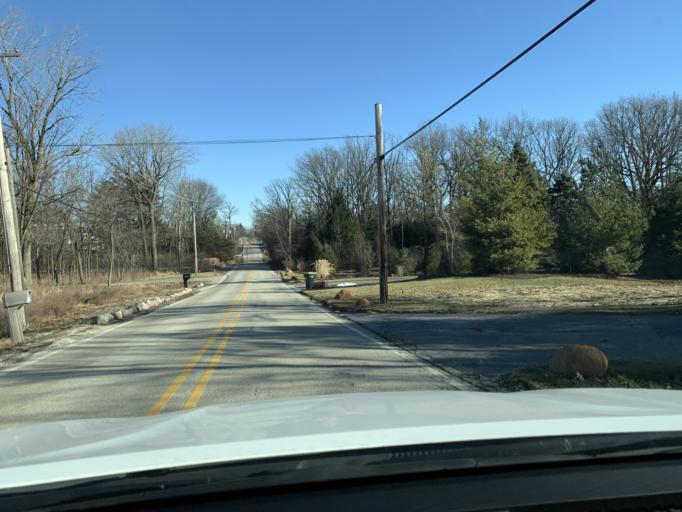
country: US
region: Illinois
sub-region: DuPage County
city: Burr Ridge
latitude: 41.7311
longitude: -87.9185
